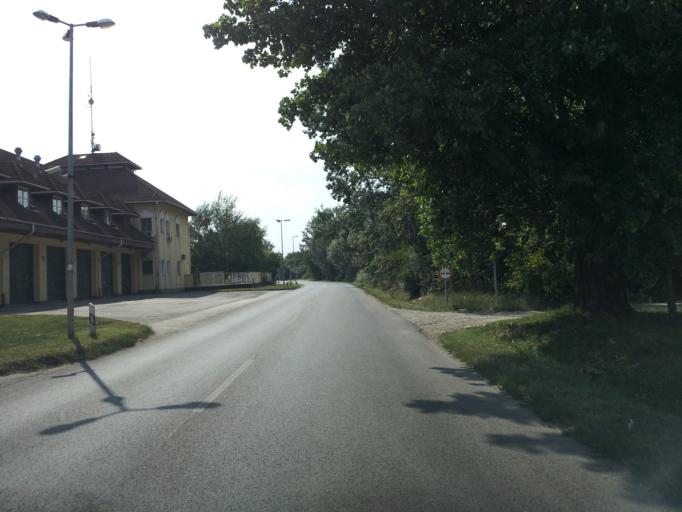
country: HU
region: Pest
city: Szigethalom
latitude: 47.3376
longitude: 19.0203
